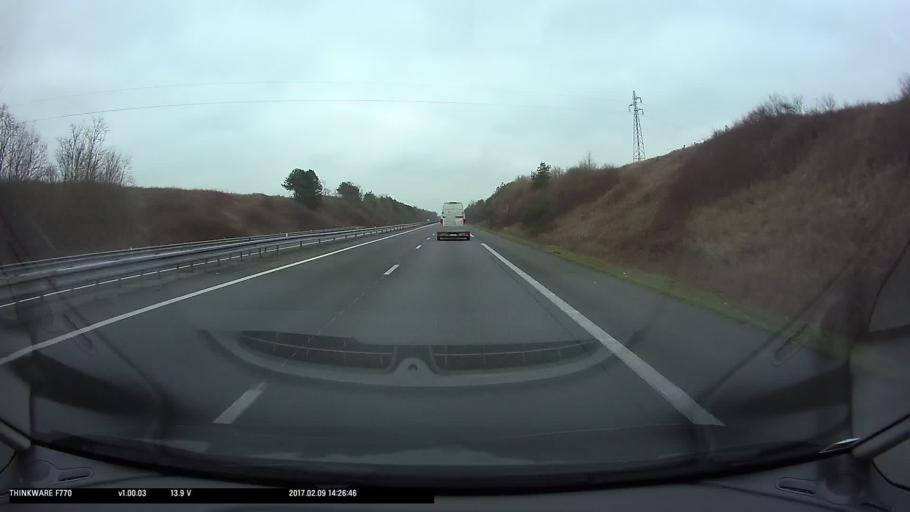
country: FR
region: Centre
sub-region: Departement du Cher
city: Foecy
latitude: 47.1632
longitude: 2.1822
